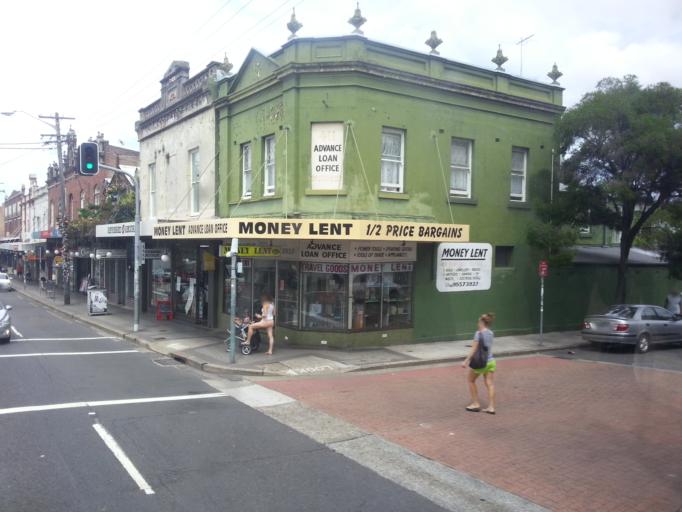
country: AU
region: New South Wales
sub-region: Marrickville
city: Newtown
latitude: -33.9002
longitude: 151.1781
